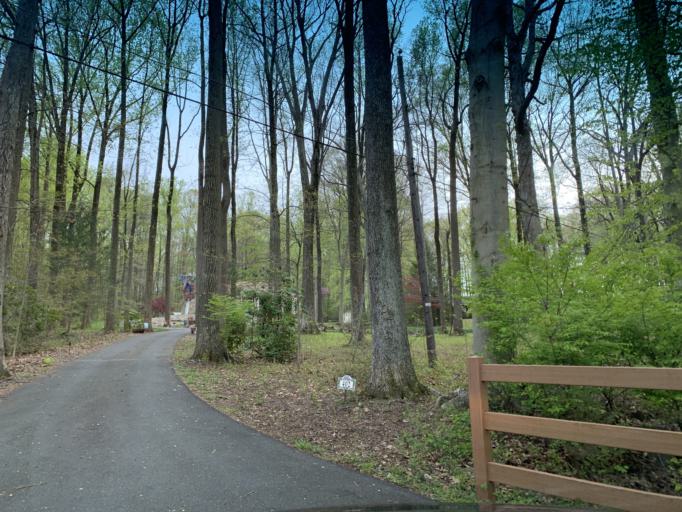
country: US
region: Maryland
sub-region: Harford County
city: Pleasant Hills
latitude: 39.4974
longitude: -76.3785
